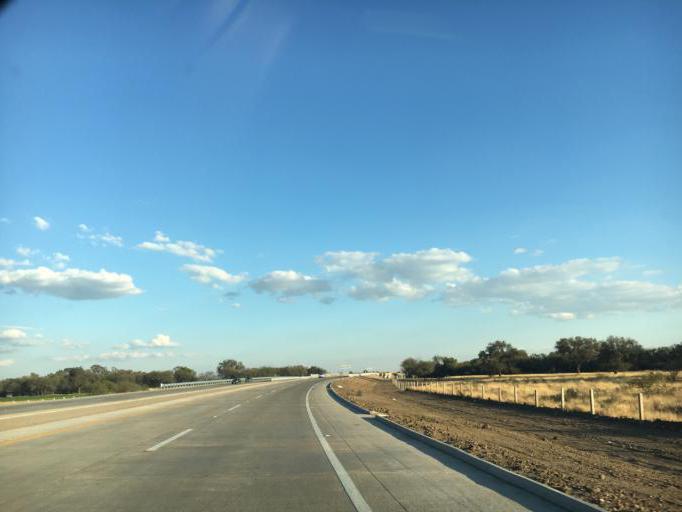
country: MX
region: Guanajuato
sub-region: Leon
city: Ladrilleras del Refugio
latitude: 21.0949
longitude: -101.5652
